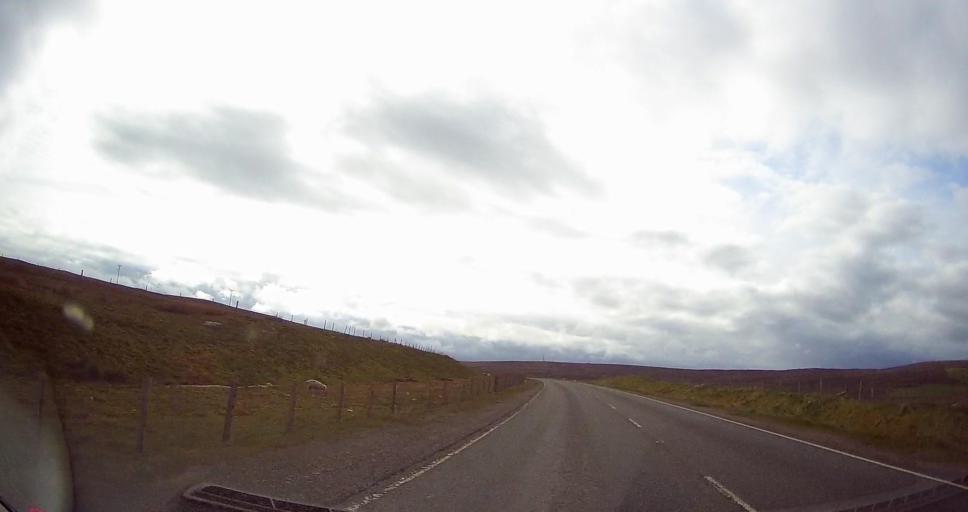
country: GB
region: Scotland
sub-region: Shetland Islands
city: Lerwick
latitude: 60.4460
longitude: -1.2500
